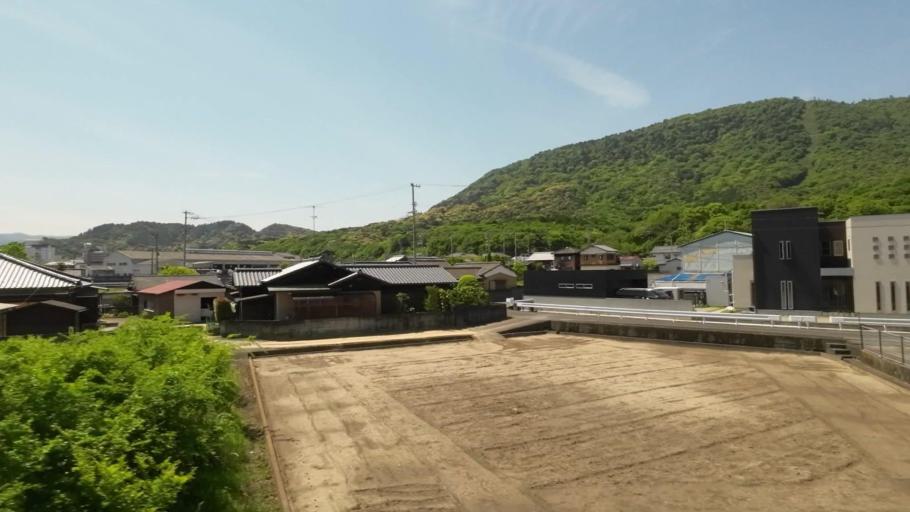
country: JP
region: Kagawa
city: Marugame
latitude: 34.1982
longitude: 133.8119
